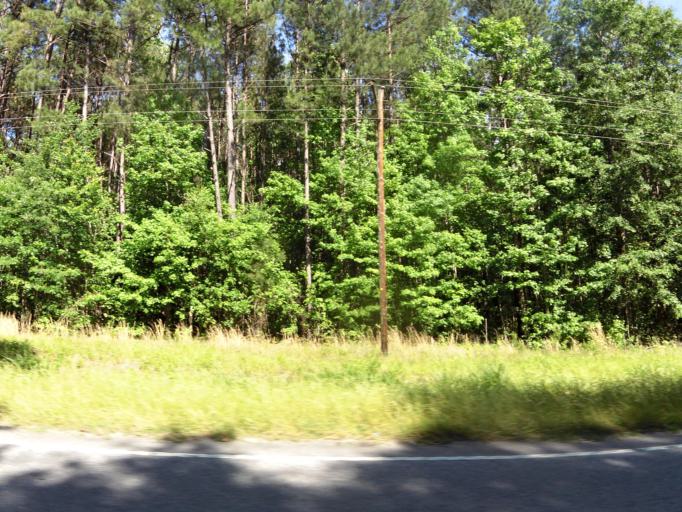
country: US
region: South Carolina
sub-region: Bamberg County
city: Denmark
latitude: 33.2690
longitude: -81.1548
